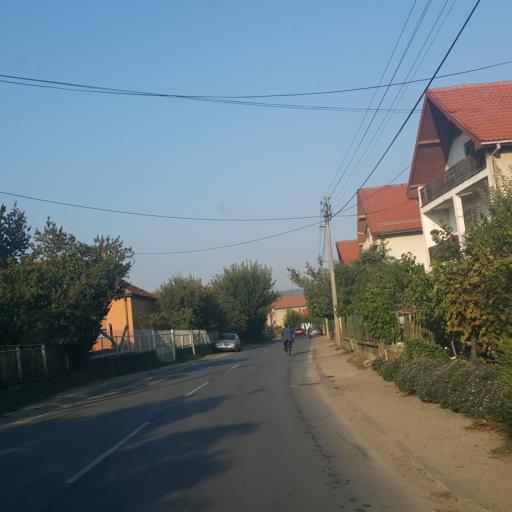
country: RS
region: Central Serbia
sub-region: Zajecarski Okrug
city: Zajecar
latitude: 43.9115
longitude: 22.2630
